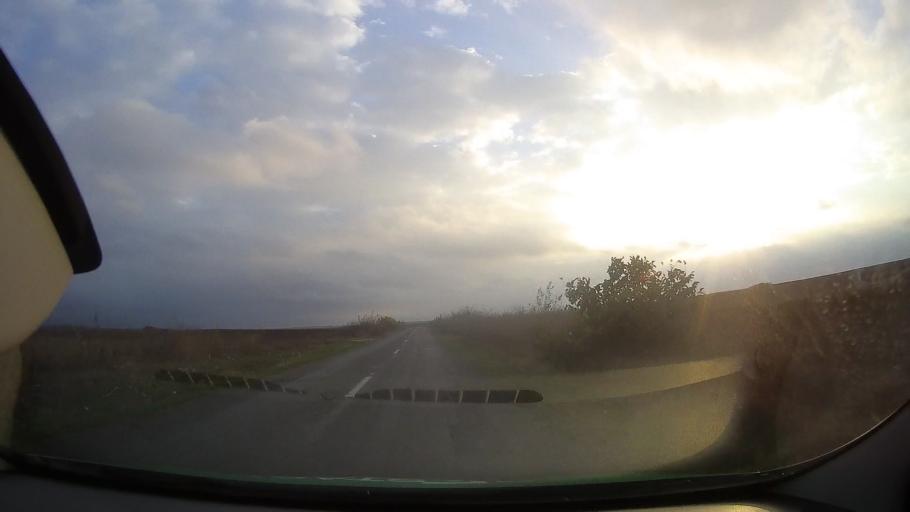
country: RO
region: Constanta
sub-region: Comuna Adamclisi
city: Adamclisi
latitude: 44.0225
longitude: 27.9075
